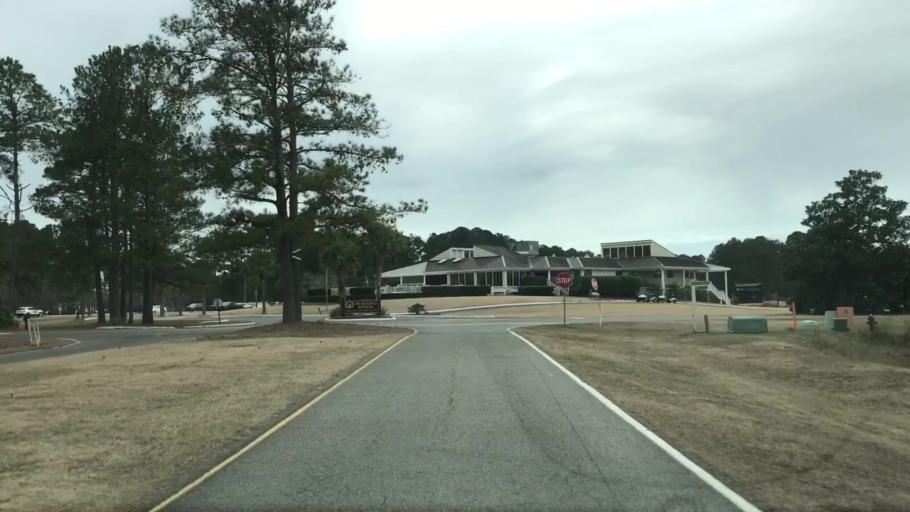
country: US
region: South Carolina
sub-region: Horry County
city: Red Hill
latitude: 33.7771
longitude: -79.0033
